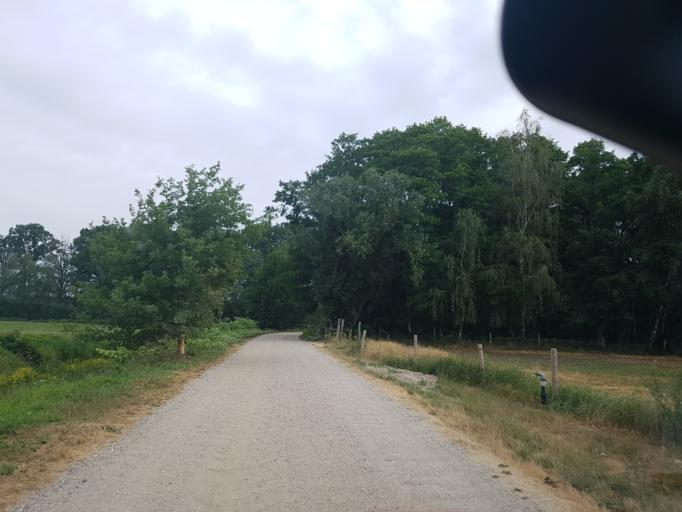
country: DE
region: Brandenburg
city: Schonewalde
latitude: 51.7002
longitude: 13.5408
